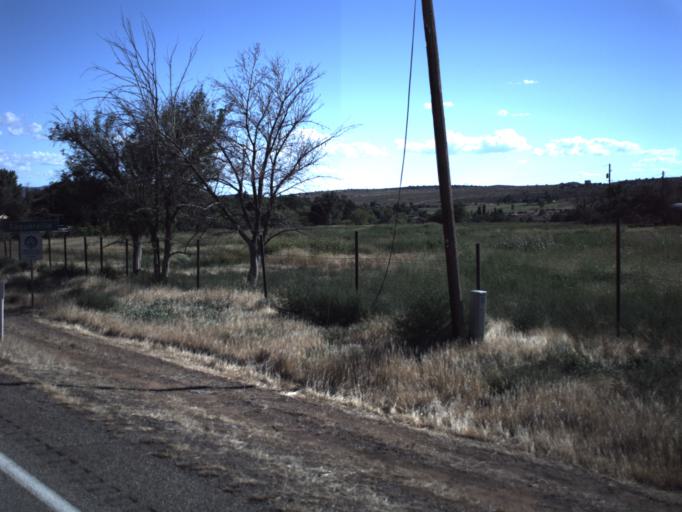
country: US
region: Utah
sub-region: Washington County
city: Toquerville
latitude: 37.2590
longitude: -113.2863
